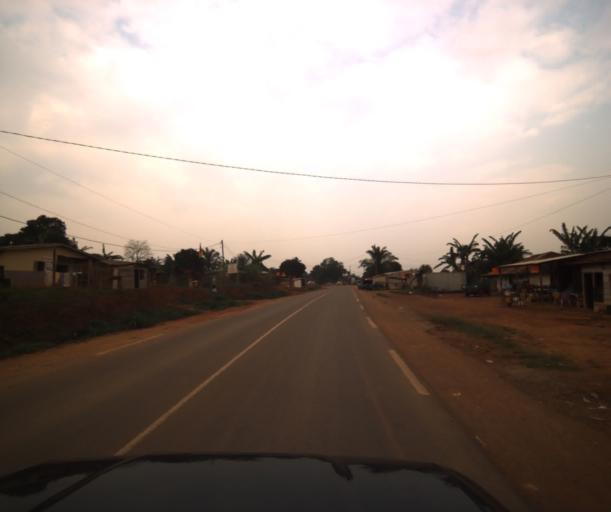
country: CM
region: Centre
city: Mbankomo
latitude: 3.8024
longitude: 11.4620
